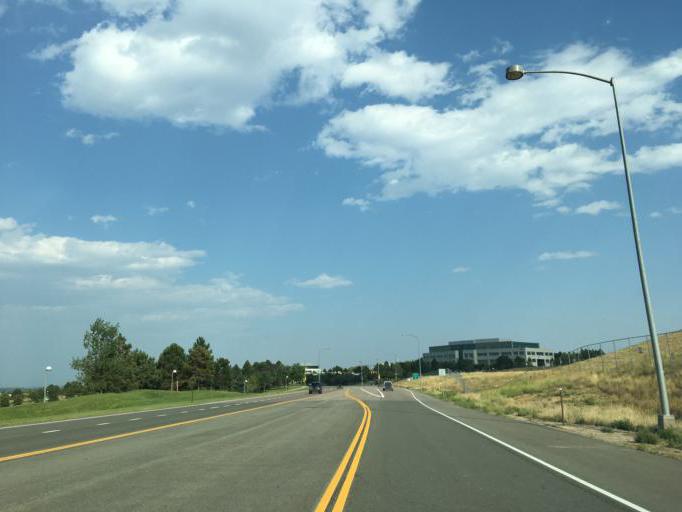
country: US
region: Colorado
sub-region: Broomfield County
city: Broomfield
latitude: 39.9171
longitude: -105.1271
